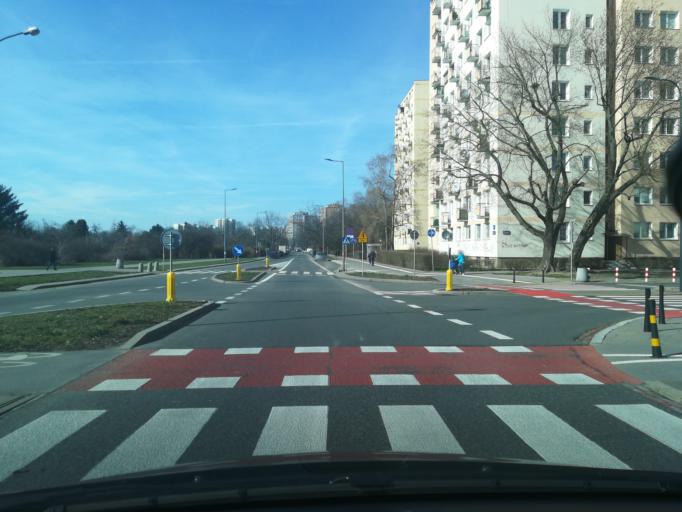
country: PL
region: Masovian Voivodeship
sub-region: Warszawa
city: Praga Poludnie
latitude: 52.2360
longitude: 21.0769
